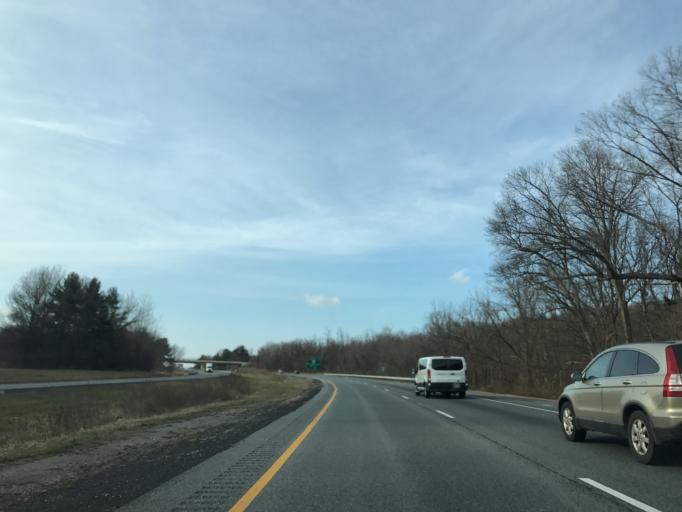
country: US
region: Pennsylvania
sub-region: York County
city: New Freedom
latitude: 39.7010
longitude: -76.6407
